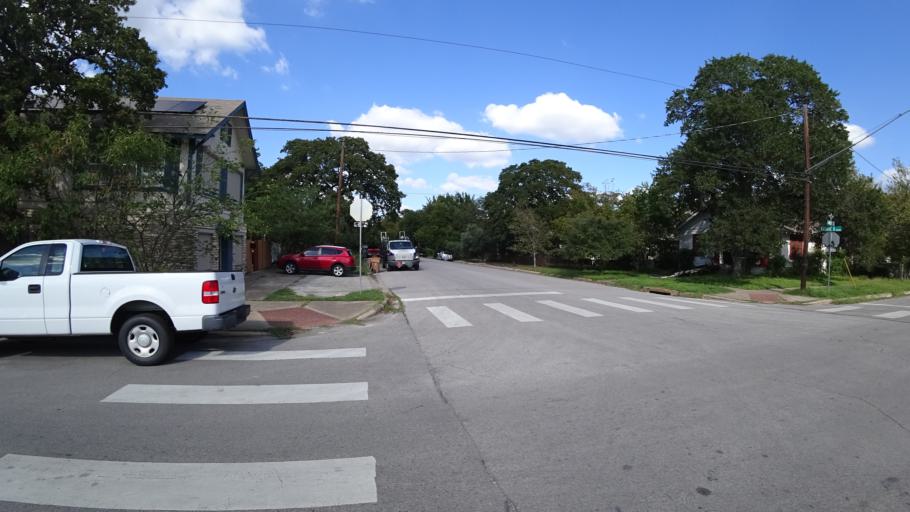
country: US
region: Texas
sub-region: Travis County
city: Austin
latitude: 30.3044
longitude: -97.7348
